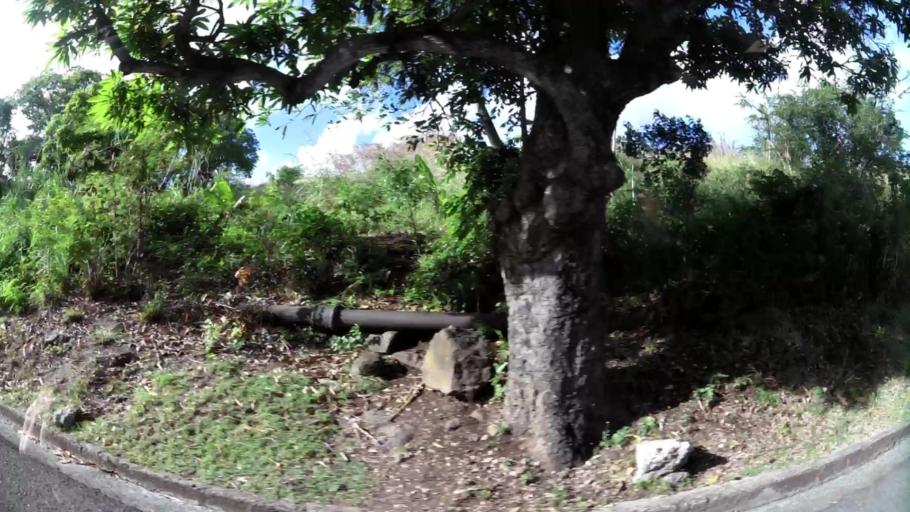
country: AG
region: Saint Peter
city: All Saints
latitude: 17.0456
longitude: -61.8154
